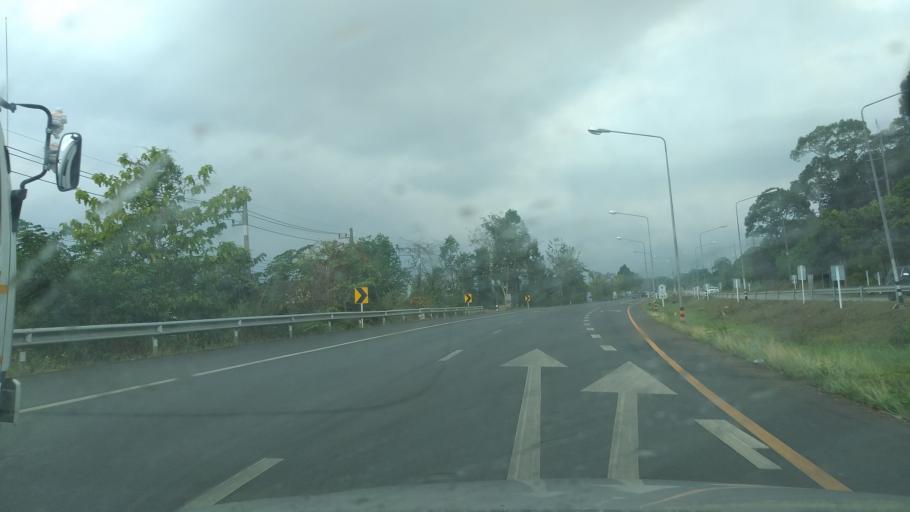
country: TH
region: Chanthaburi
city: Khlung
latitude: 12.4314
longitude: 102.3108
